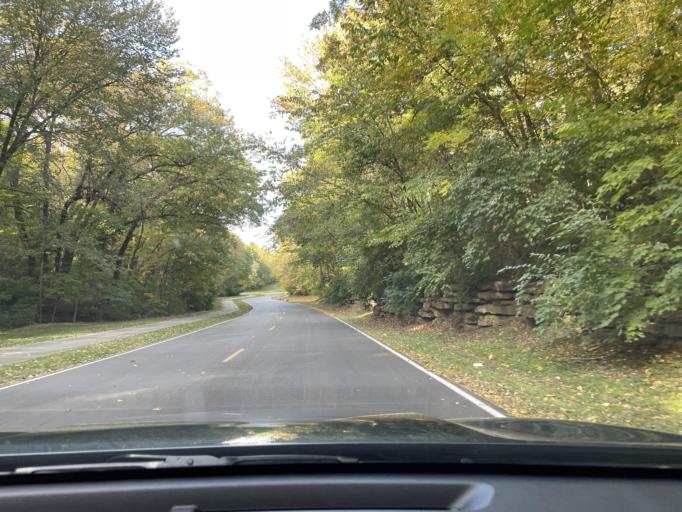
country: US
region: Kansas
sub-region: Doniphan County
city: Elwood
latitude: 39.7216
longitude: -94.8449
